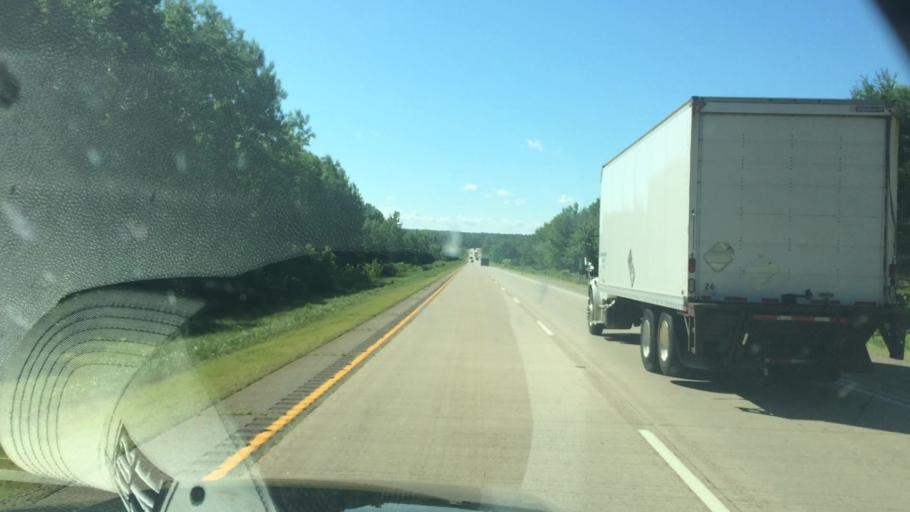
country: US
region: Wisconsin
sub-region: Marathon County
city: Mosinee
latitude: 44.7010
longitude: -89.6514
